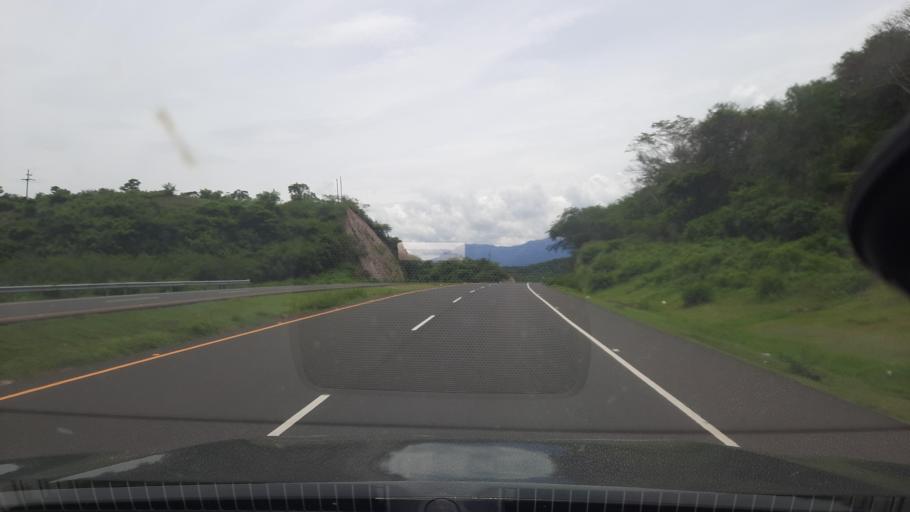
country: HN
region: Valle
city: Aramecina
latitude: 13.6805
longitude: -87.7294
